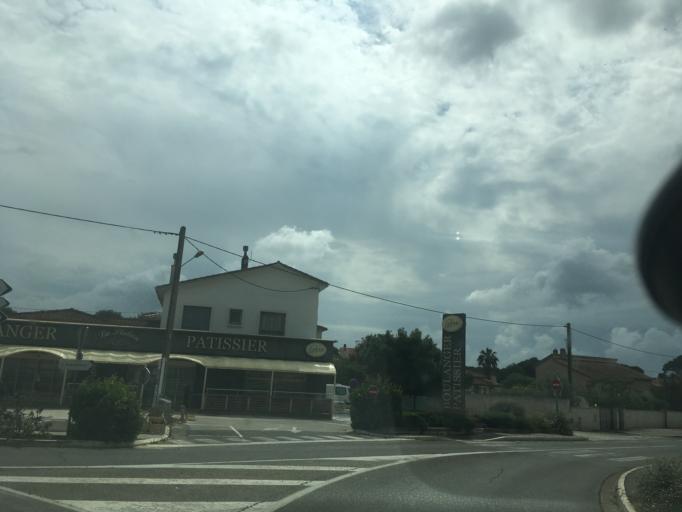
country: FR
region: Provence-Alpes-Cote d'Azur
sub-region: Departement du Var
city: La Londe-les-Maures
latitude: 43.1343
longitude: 6.2372
